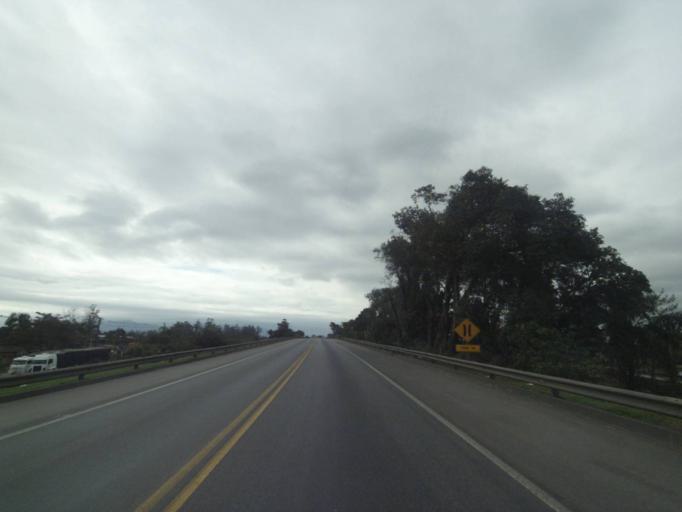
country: BR
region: Parana
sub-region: Paranagua
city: Paranagua
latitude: -25.5525
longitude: -48.5619
